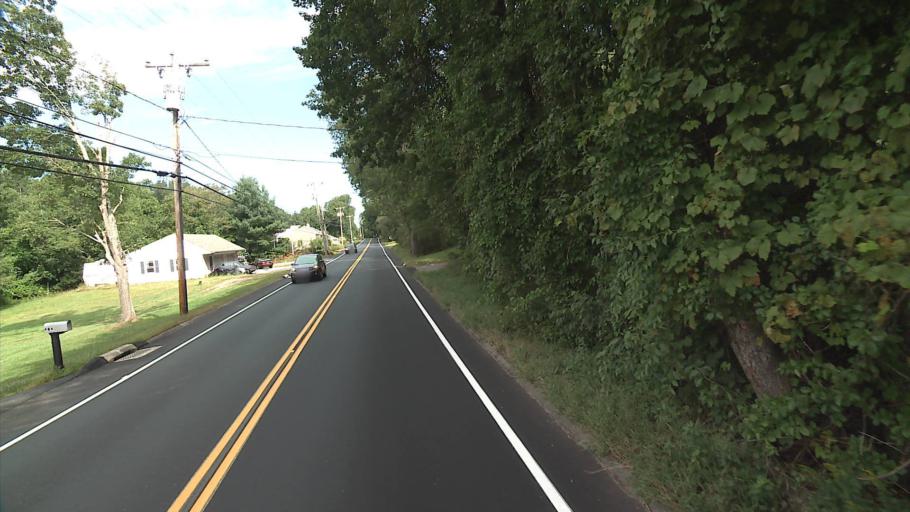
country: US
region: Connecticut
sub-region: Tolland County
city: Tolland
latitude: 41.8610
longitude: -72.3015
